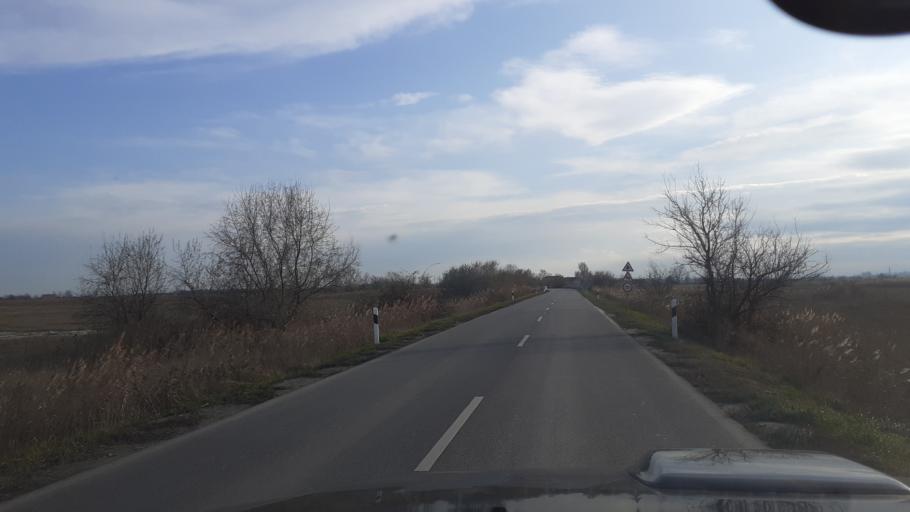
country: HU
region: Bacs-Kiskun
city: Kunszentmiklos
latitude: 47.0518
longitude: 19.1135
